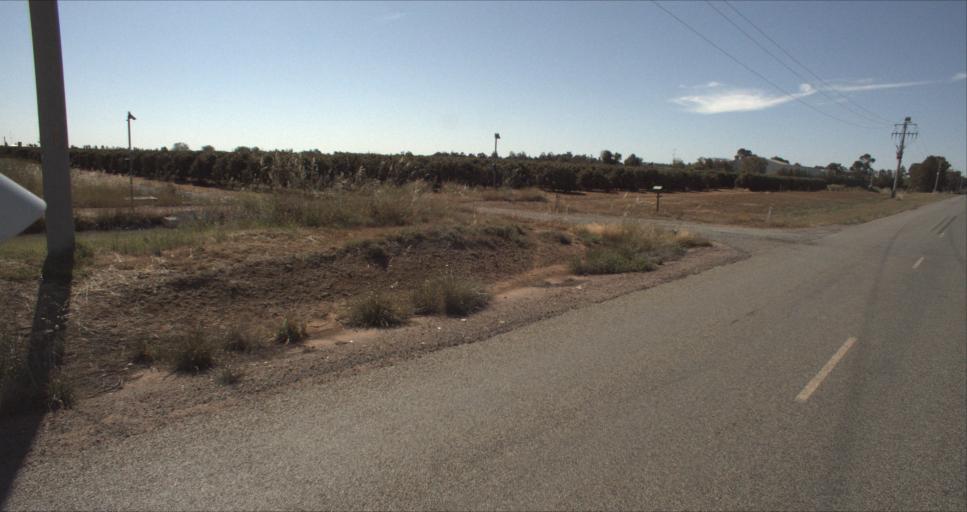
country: AU
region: New South Wales
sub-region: Leeton
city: Leeton
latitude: -34.5619
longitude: 146.3834
